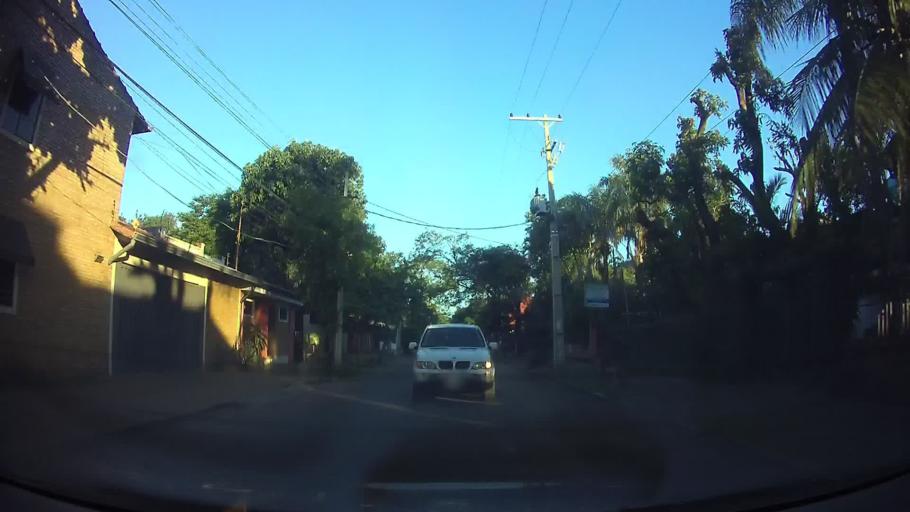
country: PY
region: Central
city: Fernando de la Mora
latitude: -25.3242
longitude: -57.5573
